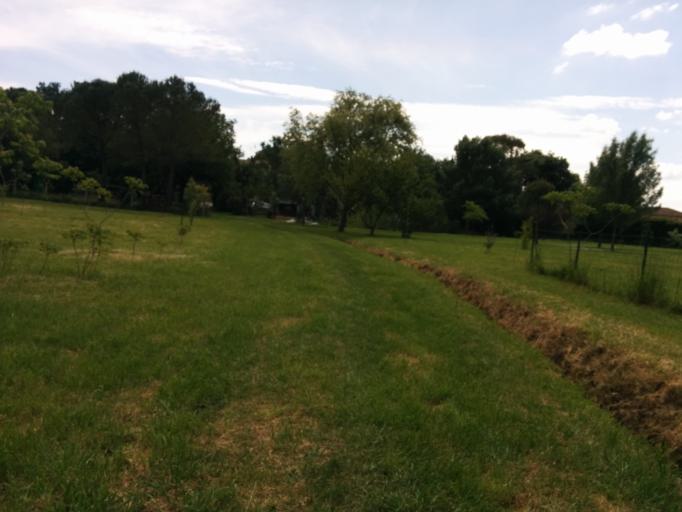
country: FR
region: Languedoc-Roussillon
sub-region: Departement du Gard
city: Saint-Christol-les-Ales
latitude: 44.0877
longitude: 4.0707
